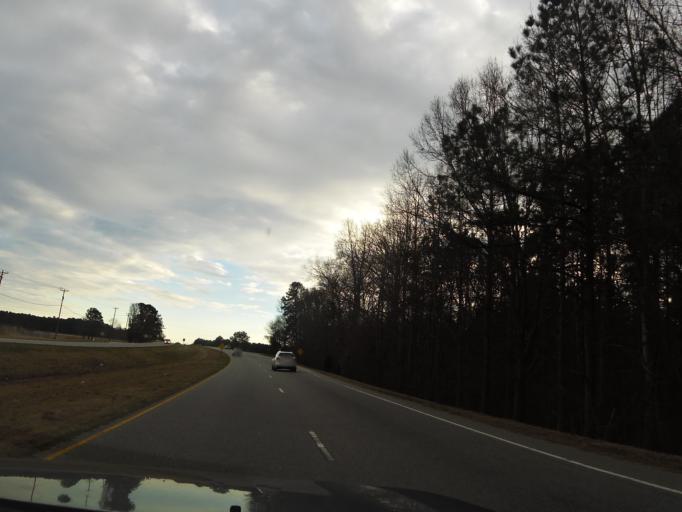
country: US
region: North Carolina
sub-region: Nash County
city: Rocky Mount
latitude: 35.9158
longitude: -77.8318
